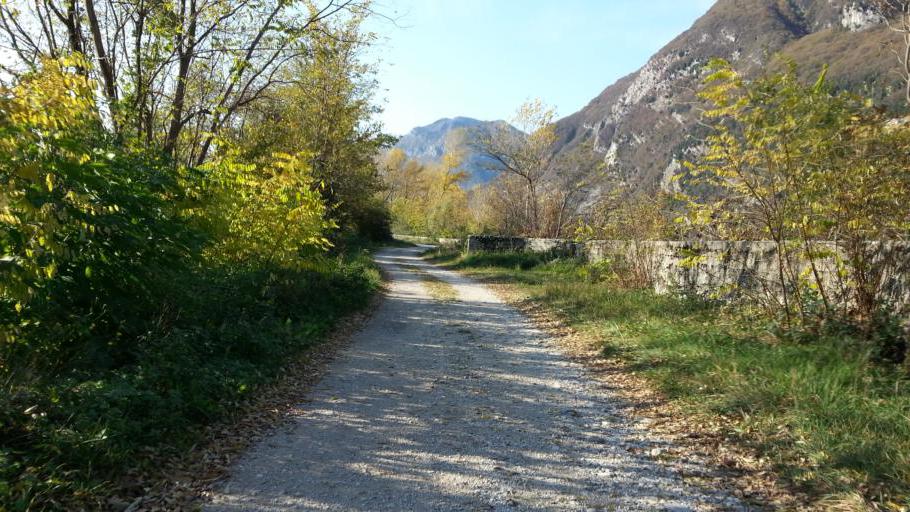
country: IT
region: Friuli Venezia Giulia
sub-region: Provincia di Udine
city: Venzone
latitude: 46.3335
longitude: 13.1331
